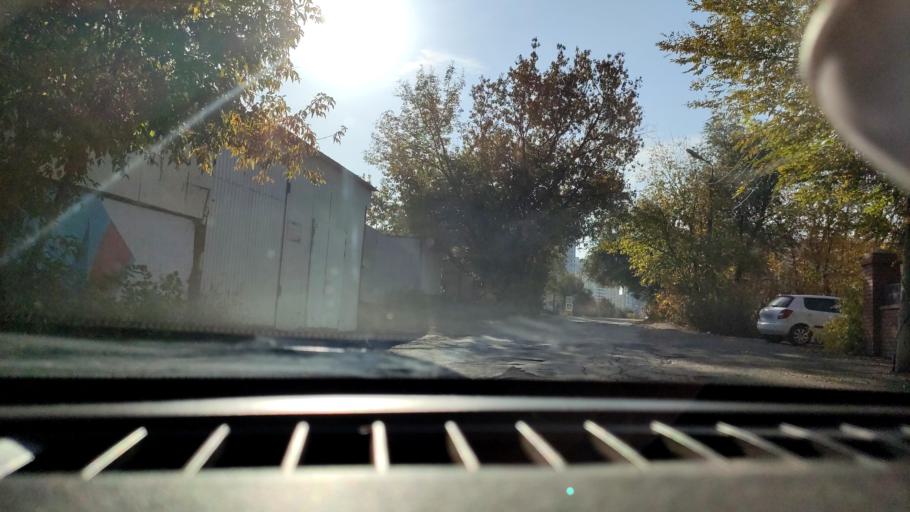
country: RU
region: Samara
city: Samara
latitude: 53.2229
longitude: 50.1649
